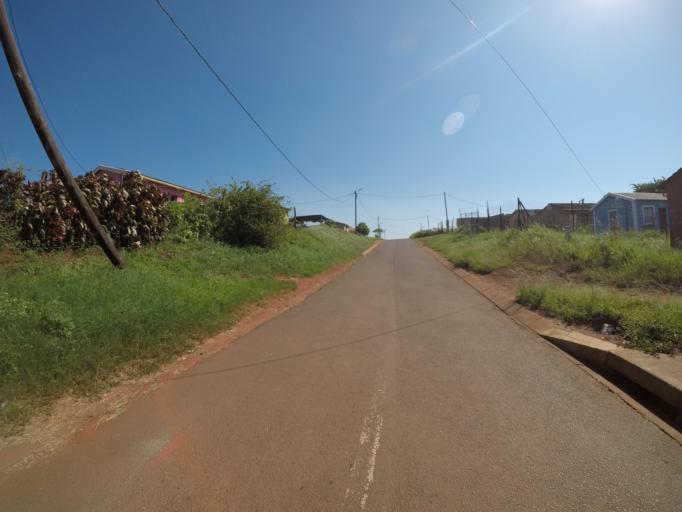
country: ZA
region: KwaZulu-Natal
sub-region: uThungulu District Municipality
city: Empangeni
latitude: -28.7716
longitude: 31.8794
